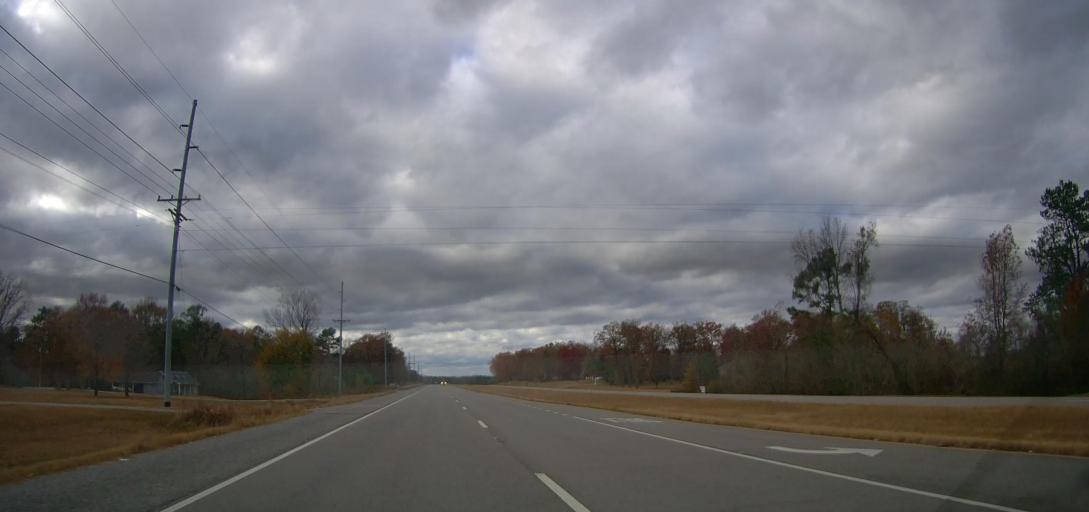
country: US
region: Alabama
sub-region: Lawrence County
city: Town Creek
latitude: 34.5682
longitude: -87.3759
